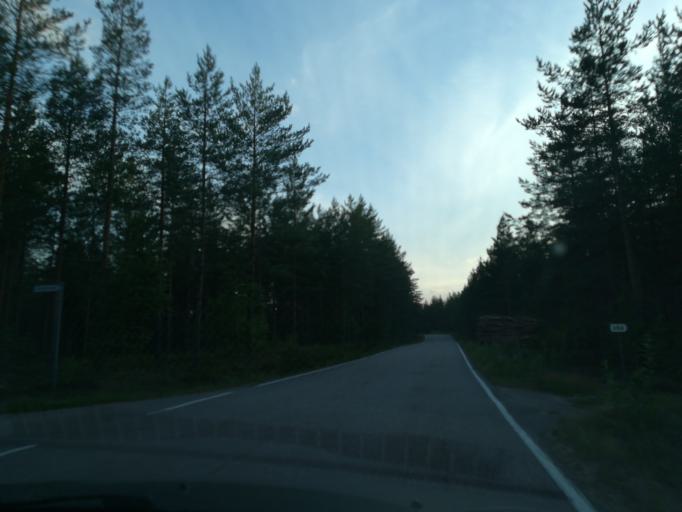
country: FI
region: South Karelia
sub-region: Lappeenranta
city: Joutseno
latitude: 61.3451
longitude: 28.4157
